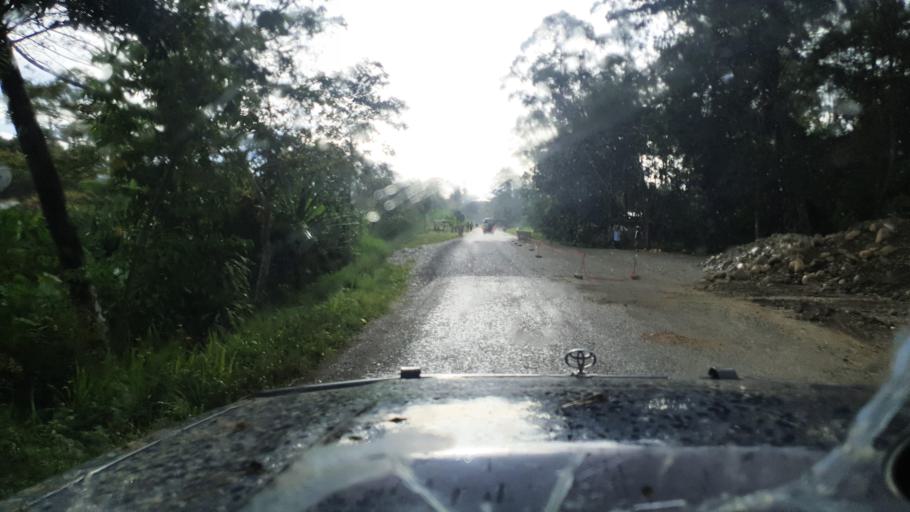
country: PG
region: Jiwaka
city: Minj
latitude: -5.9277
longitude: 144.7920
